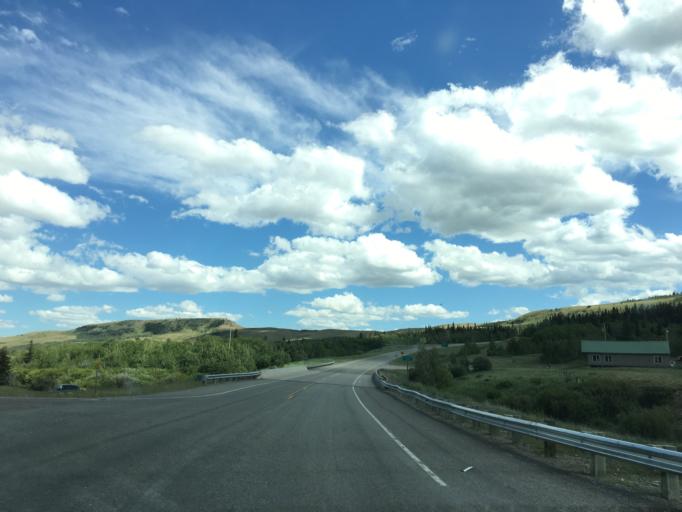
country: US
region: Montana
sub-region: Glacier County
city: Browning
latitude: 48.6091
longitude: -113.2877
